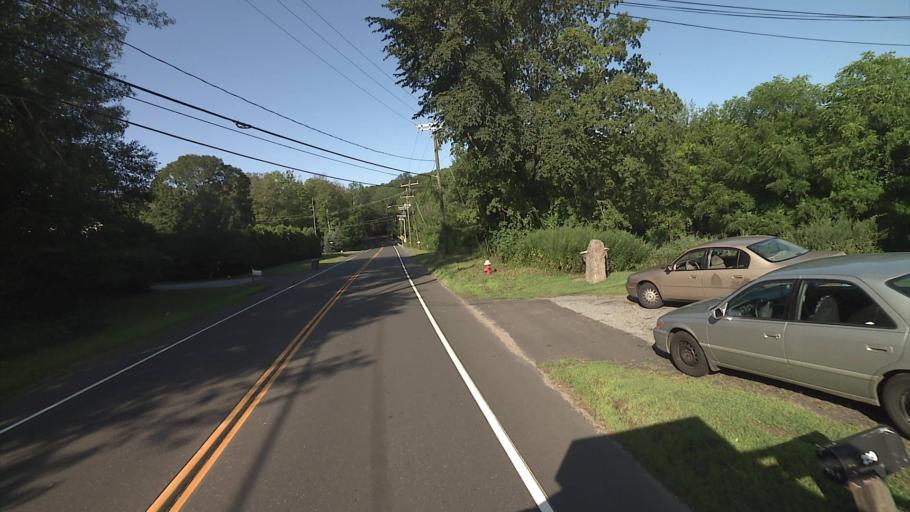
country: US
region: Connecticut
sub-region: New London County
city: Niantic
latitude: 41.3658
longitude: -72.2323
